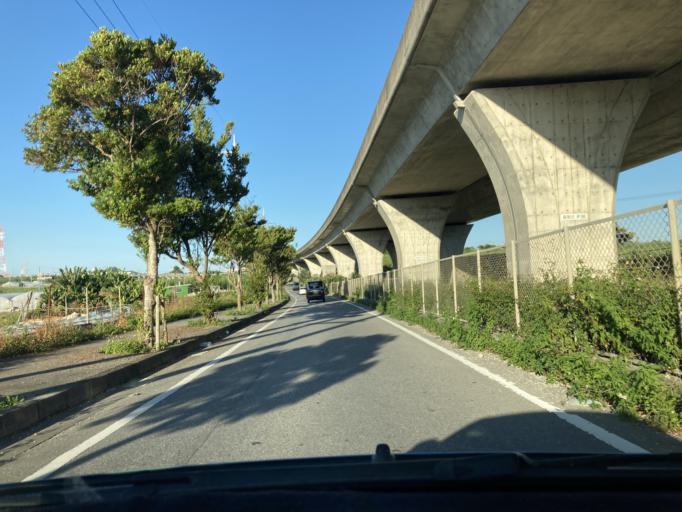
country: JP
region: Okinawa
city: Tomigusuku
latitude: 26.1839
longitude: 127.7344
